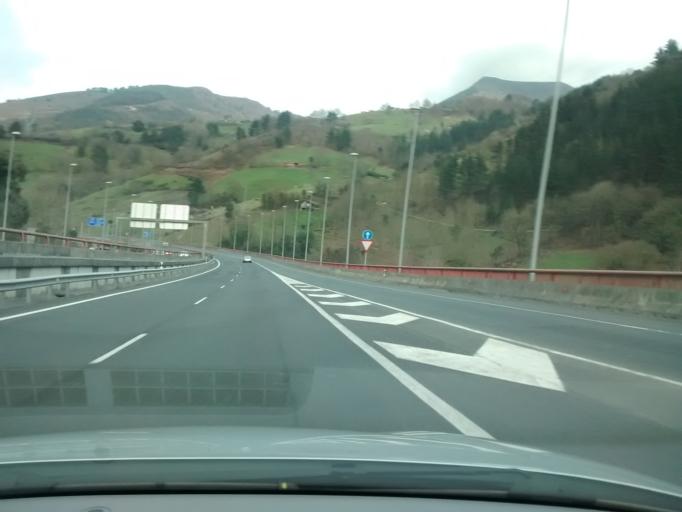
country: ES
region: Basque Country
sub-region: Bizkaia
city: Gordexola
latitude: 43.1941
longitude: -3.0453
